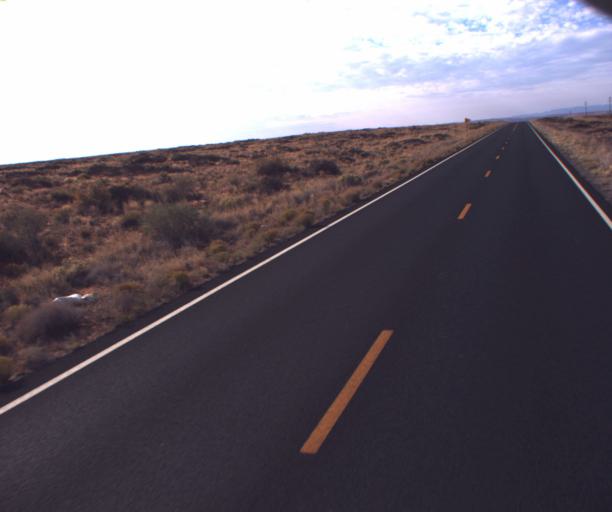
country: US
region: Arizona
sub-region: Apache County
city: Many Farms
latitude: 36.8602
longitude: -109.6356
